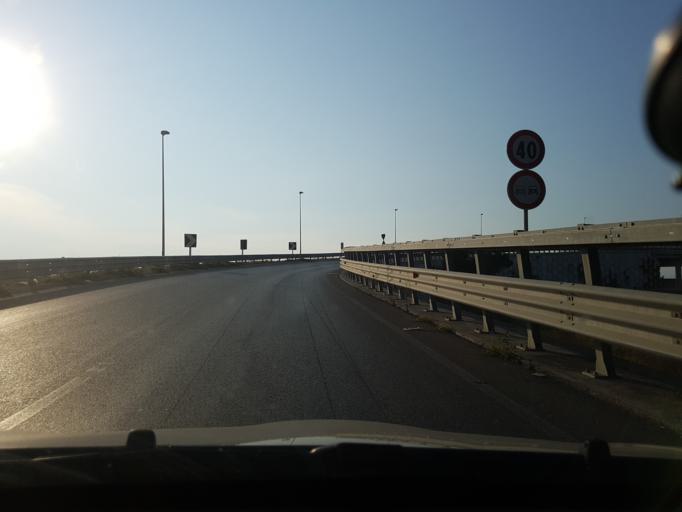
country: IT
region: Apulia
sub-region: Provincia di Foggia
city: Cerignola
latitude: 41.2738
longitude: 15.8753
